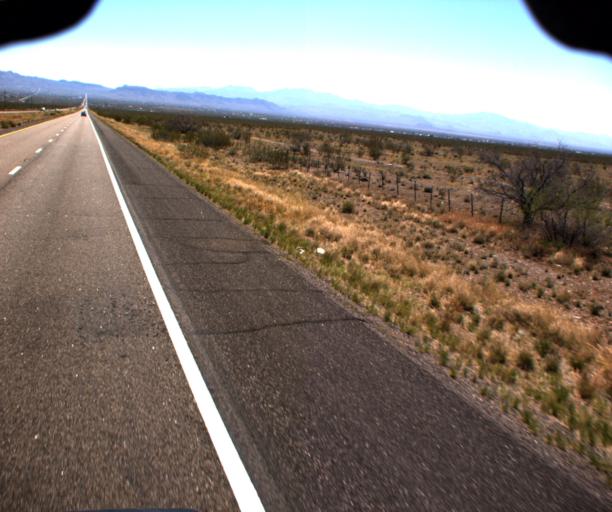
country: US
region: Arizona
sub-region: Mohave County
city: Golden Valley
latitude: 35.2274
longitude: -114.3304
